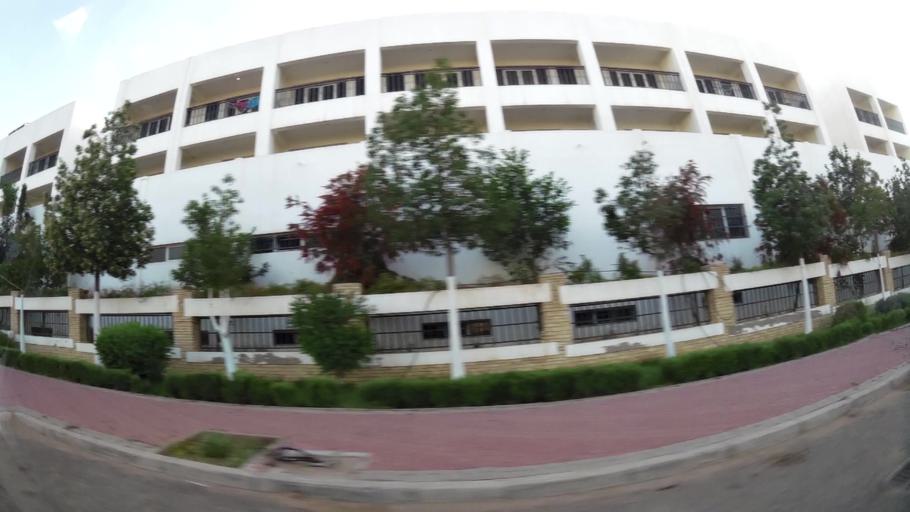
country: MA
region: Souss-Massa-Draa
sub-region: Agadir-Ida-ou-Tnan
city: Agadir
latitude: 30.4023
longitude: -9.5926
